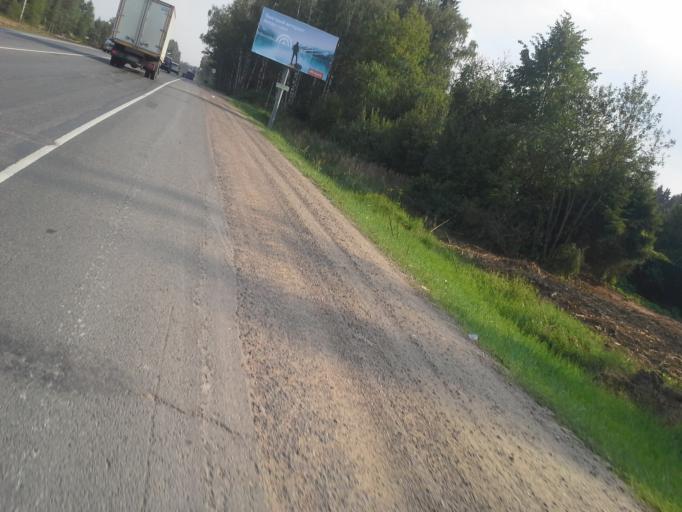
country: RU
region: Moskovskaya
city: Snegiri
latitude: 55.8916
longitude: 36.9443
